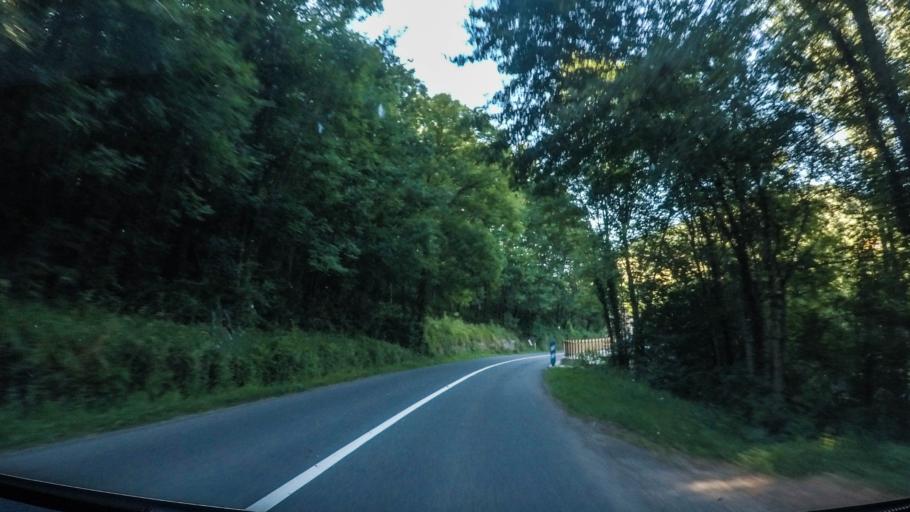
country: FR
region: Midi-Pyrenees
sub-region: Departement de l'Aveyron
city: Marcillac-Vallon
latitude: 44.4761
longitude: 2.4533
